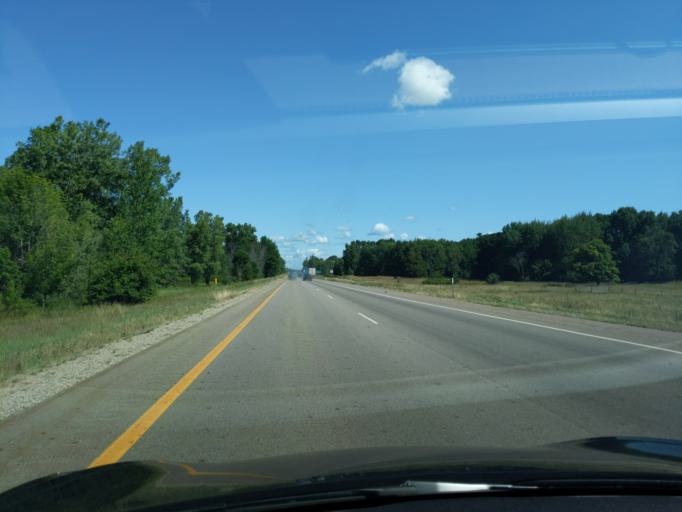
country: US
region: Michigan
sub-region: Gratiot County
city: Ithaca
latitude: 43.3260
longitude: -84.6010
